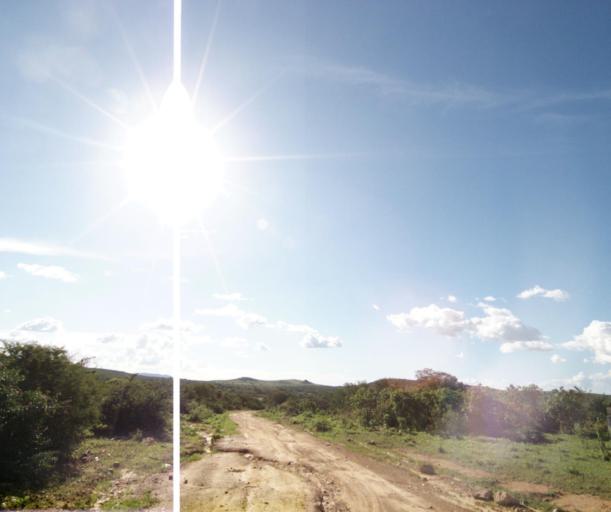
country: BR
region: Bahia
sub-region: Tanhacu
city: Tanhacu
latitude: -14.1878
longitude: -40.9440
